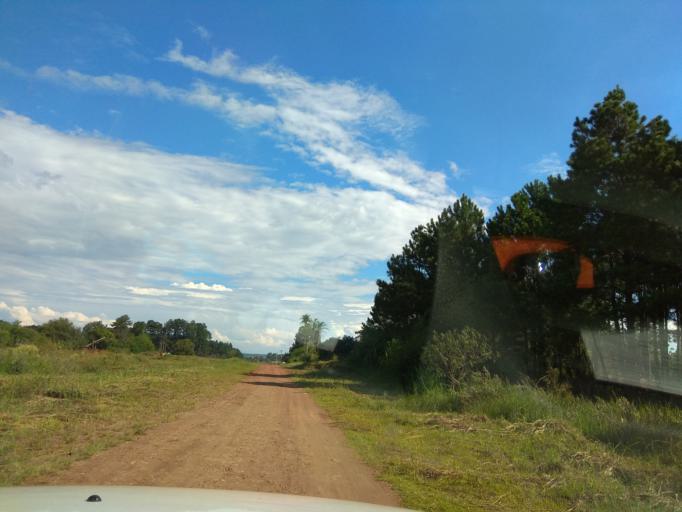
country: AR
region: Misiones
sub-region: Departamento de Candelaria
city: Candelaria
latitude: -27.4660
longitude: -55.7560
